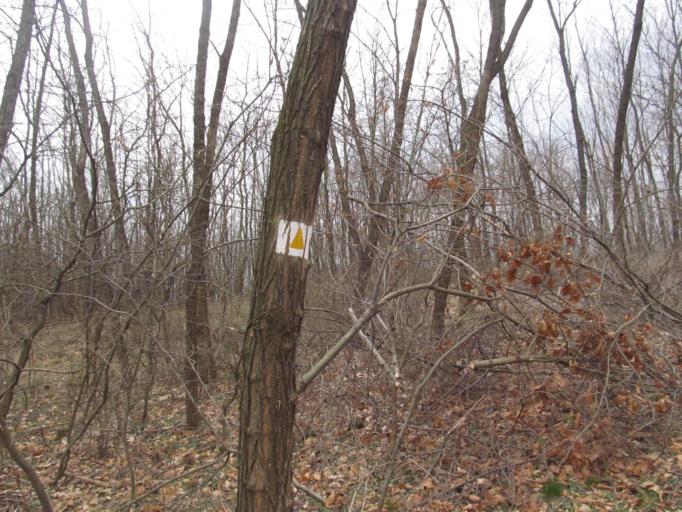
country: HU
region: Gyor-Moson-Sopron
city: Pannonhalma
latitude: 47.5319
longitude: 17.7704
